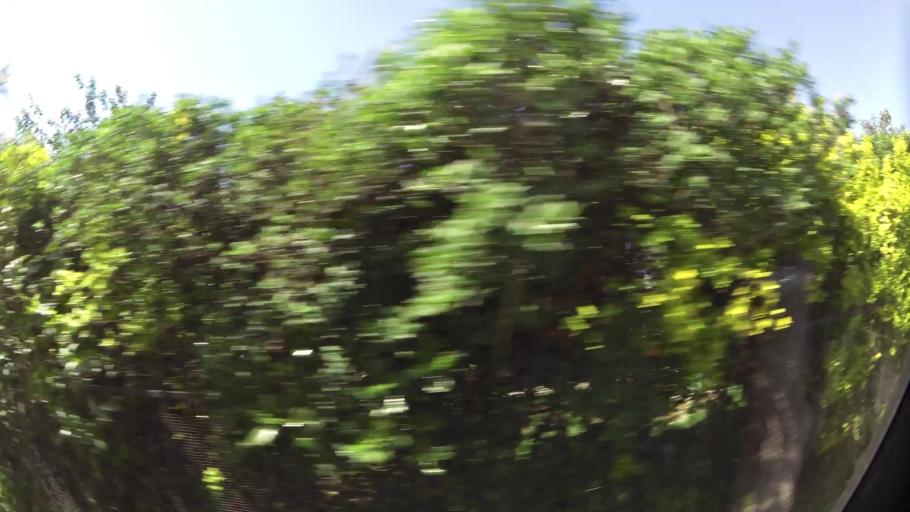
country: CL
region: Santiago Metropolitan
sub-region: Provincia de Santiago
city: Lo Prado
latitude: -33.5057
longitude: -70.7506
